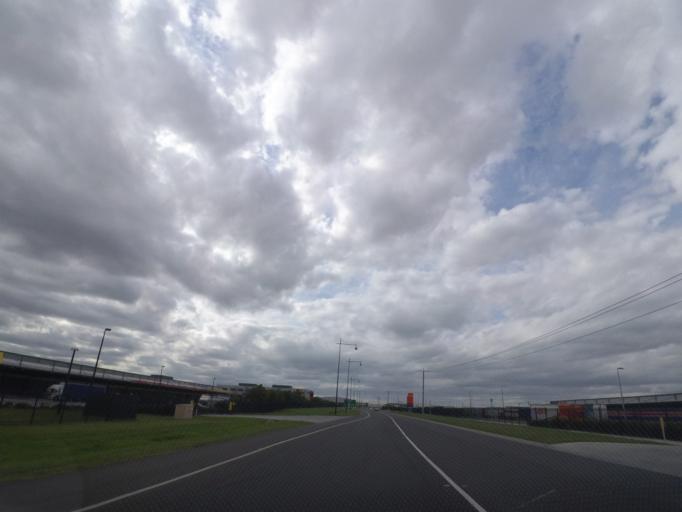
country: AU
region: Victoria
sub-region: Brimbank
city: Keilor Park
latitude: -37.6962
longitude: 144.8565
